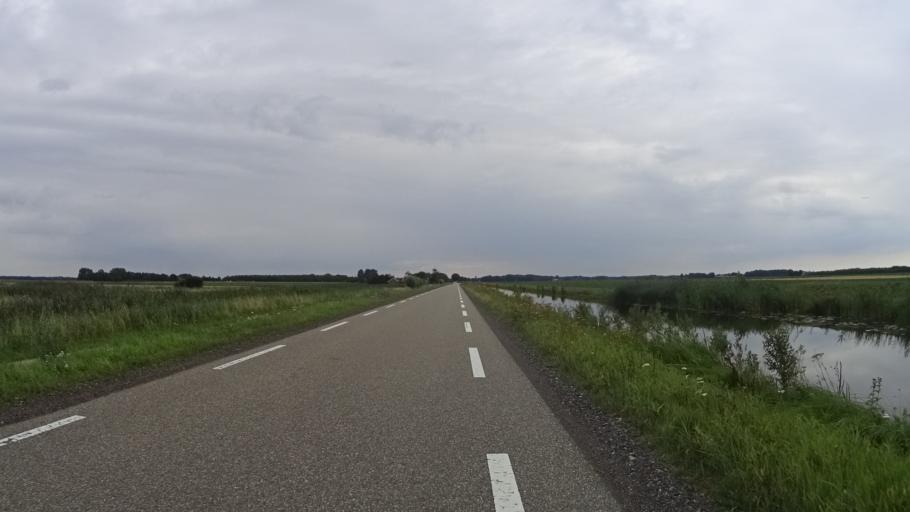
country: NL
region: Groningen
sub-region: Gemeente Slochteren
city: Slochteren
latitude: 53.2294
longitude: 6.7666
